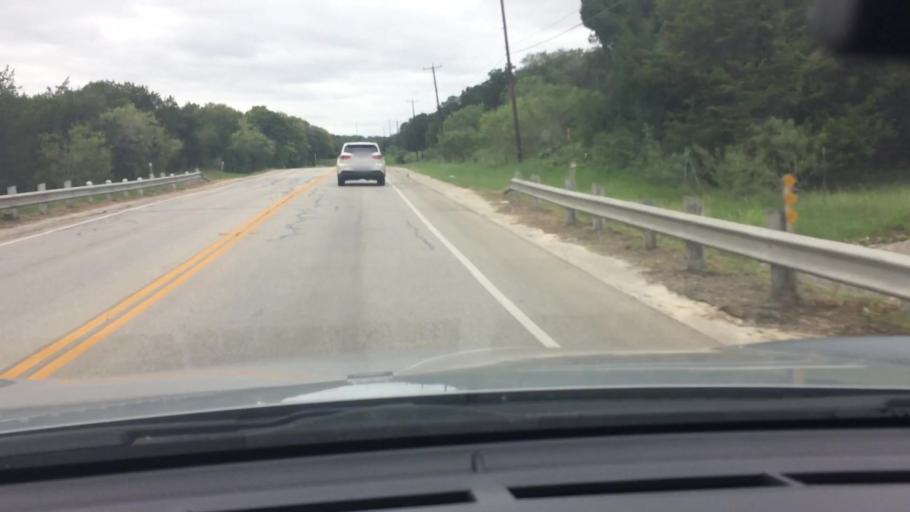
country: US
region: Texas
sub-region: Bexar County
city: Live Oak
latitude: 29.6148
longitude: -98.3597
